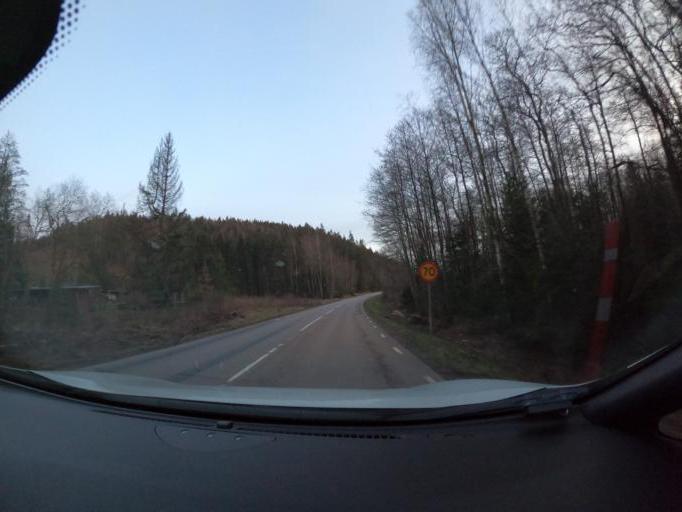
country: SE
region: Vaestra Goetaland
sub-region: Harryda Kommun
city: Landvetter
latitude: 57.6249
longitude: 12.1821
